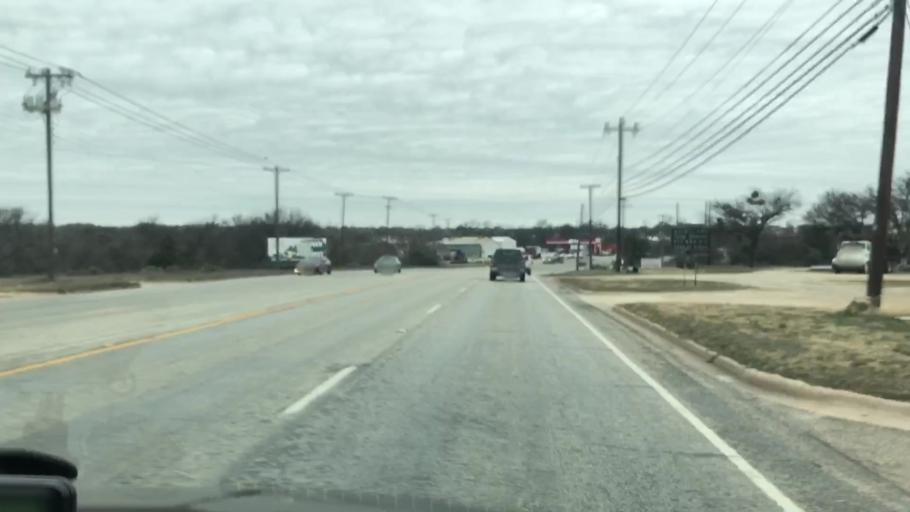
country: US
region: Texas
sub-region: Jack County
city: Jacksboro
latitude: 33.2104
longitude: -98.1575
